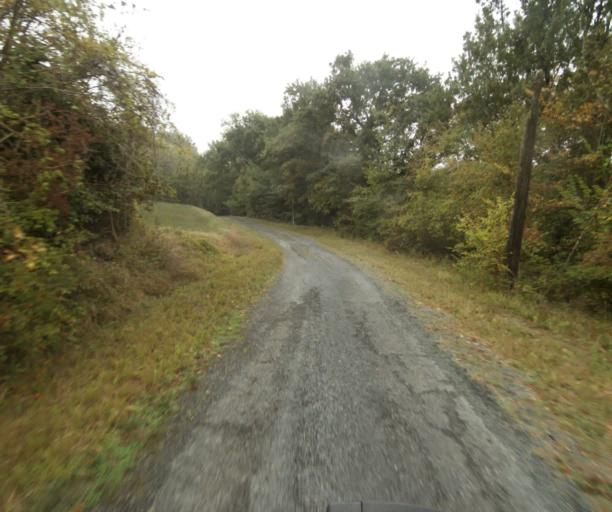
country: FR
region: Midi-Pyrenees
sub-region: Departement du Tarn-et-Garonne
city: Nohic
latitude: 43.8964
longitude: 1.4750
